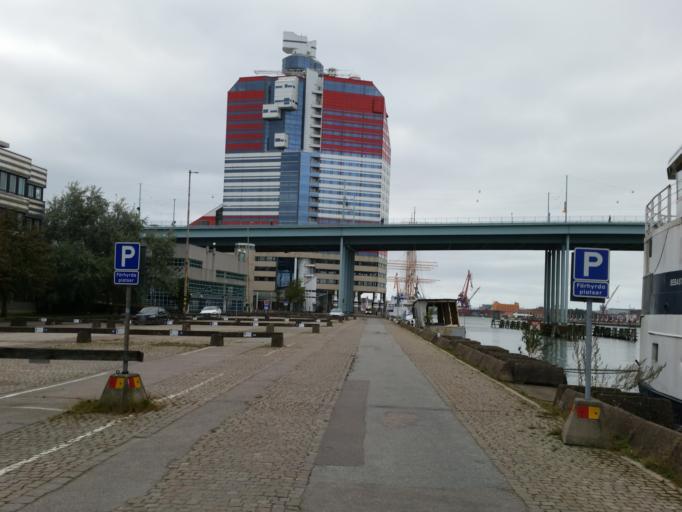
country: SE
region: Vaestra Goetaland
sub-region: Goteborg
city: Goeteborg
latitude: 57.7147
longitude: 11.9699
